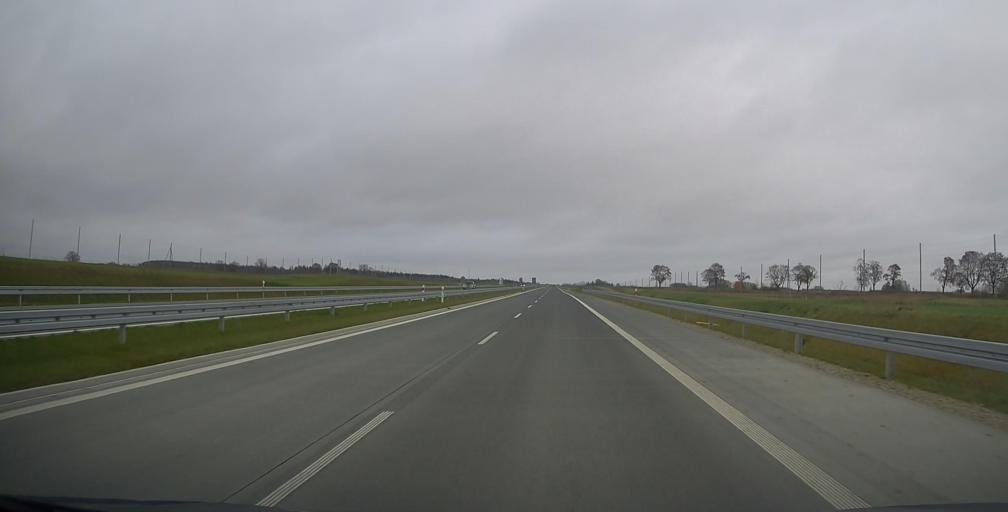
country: PL
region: Podlasie
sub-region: Powiat grajewski
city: Rajgrod
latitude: 53.8814
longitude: 22.6659
